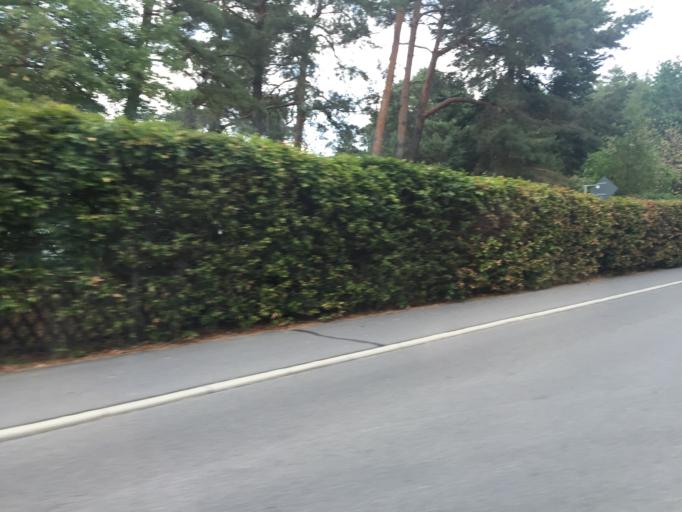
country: DE
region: Saxony
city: Schleife
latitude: 51.5296
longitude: 14.5483
